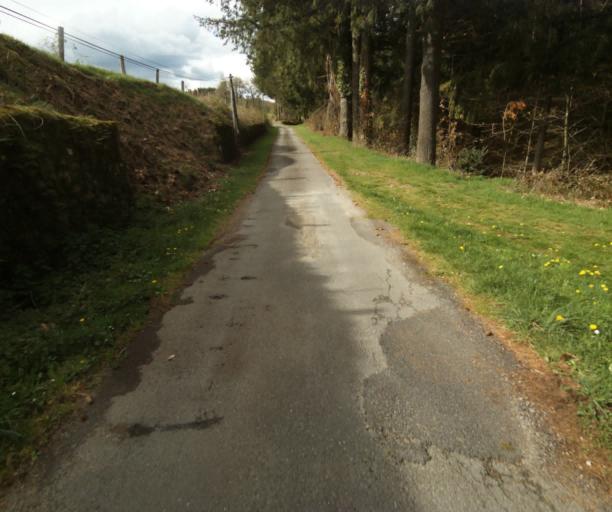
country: FR
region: Limousin
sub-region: Departement de la Correze
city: Argentat
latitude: 45.2035
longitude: 1.9684
